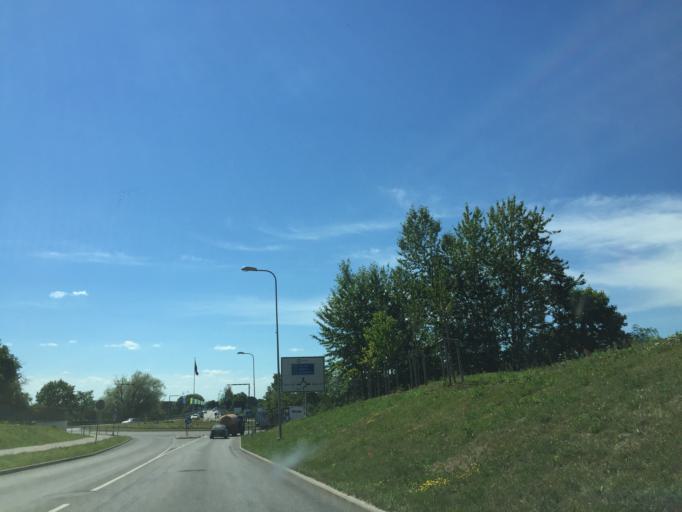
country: LV
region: Jekabpils Rajons
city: Jekabpils
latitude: 56.5028
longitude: 25.8785
